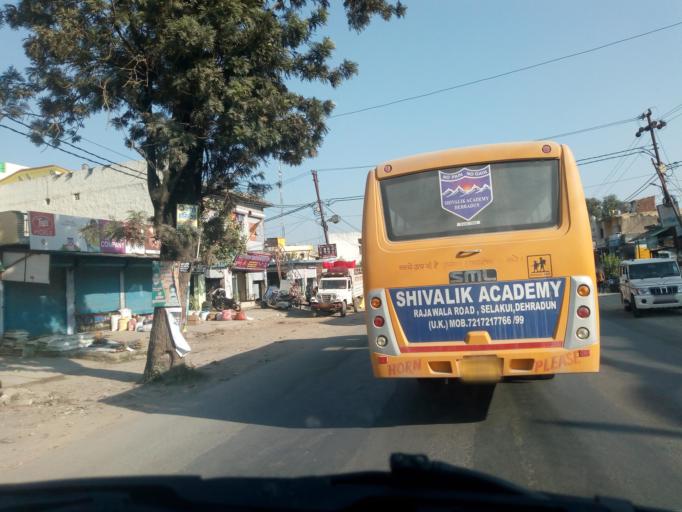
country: IN
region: Uttarakhand
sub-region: Dehradun
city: Vikasnagar
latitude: 30.3538
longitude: 77.8585
